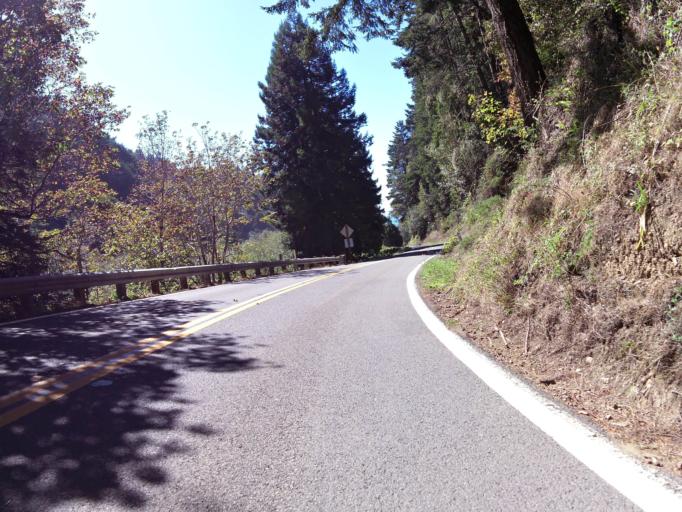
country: US
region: California
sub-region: Mendocino County
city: Fort Bragg
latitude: 39.7137
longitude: -123.8004
